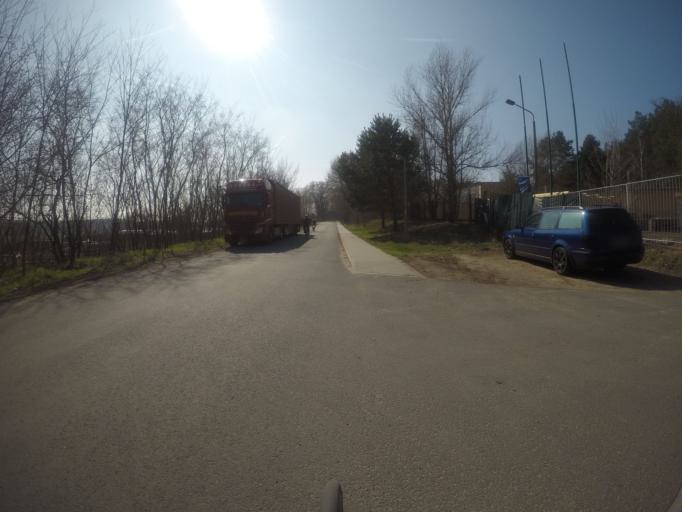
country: DE
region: Berlin
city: Muggelheim
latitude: 52.3874
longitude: 13.7024
